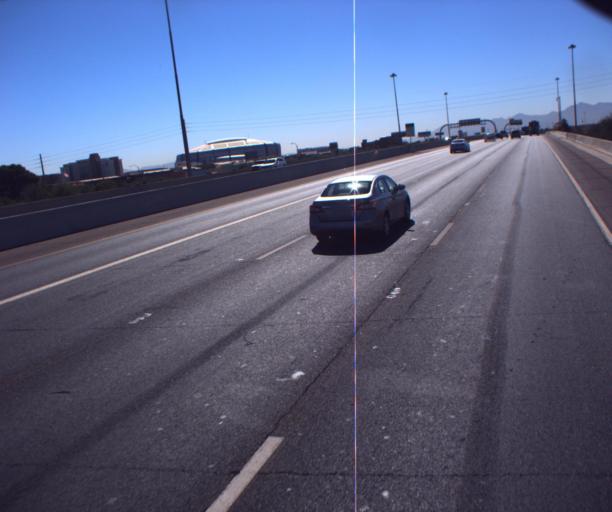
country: US
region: Arizona
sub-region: Maricopa County
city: Peoria
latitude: 33.5385
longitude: -112.2700
